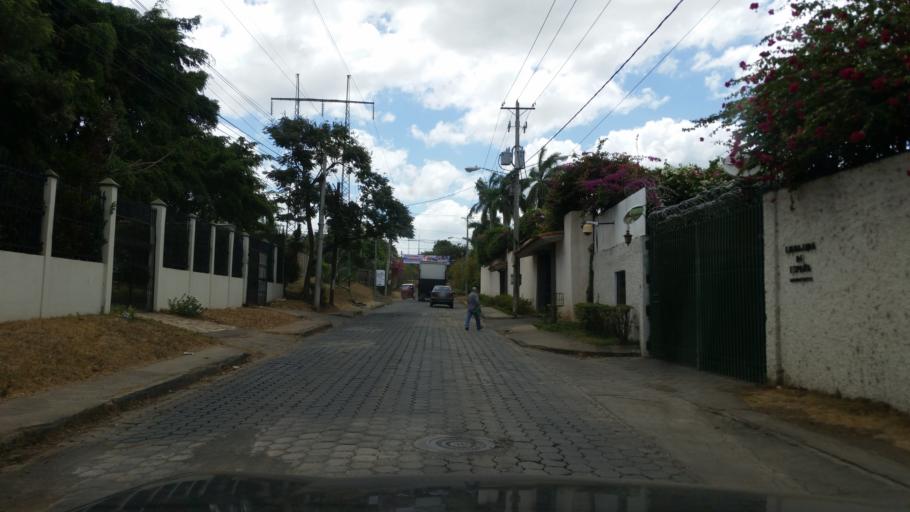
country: NI
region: Managua
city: Managua
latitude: 12.0982
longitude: -86.2325
